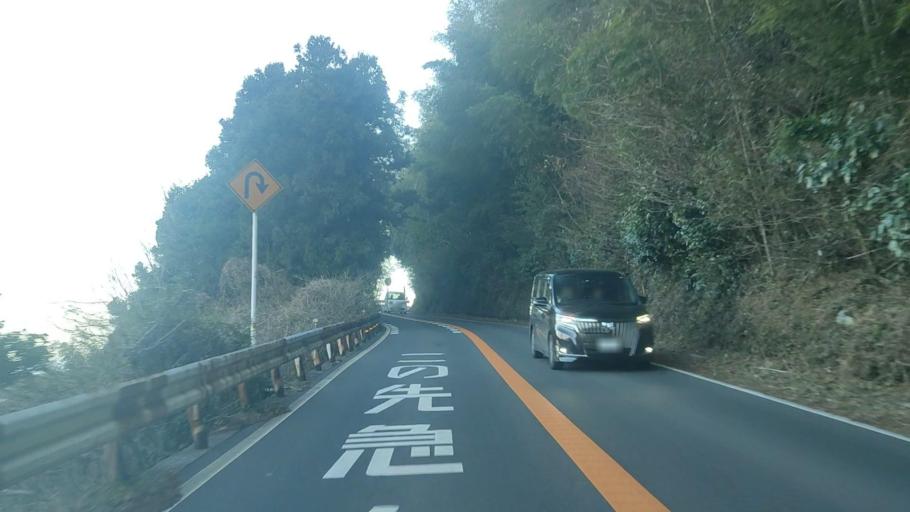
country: JP
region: Oita
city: Beppu
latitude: 33.2883
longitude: 131.4672
